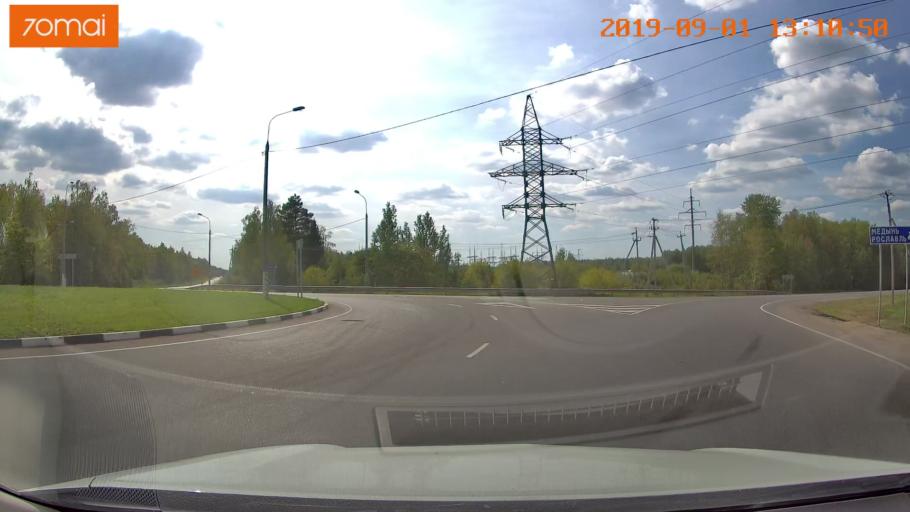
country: RU
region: Kaluga
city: Maloyaroslavets
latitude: 54.9801
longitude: 36.4257
